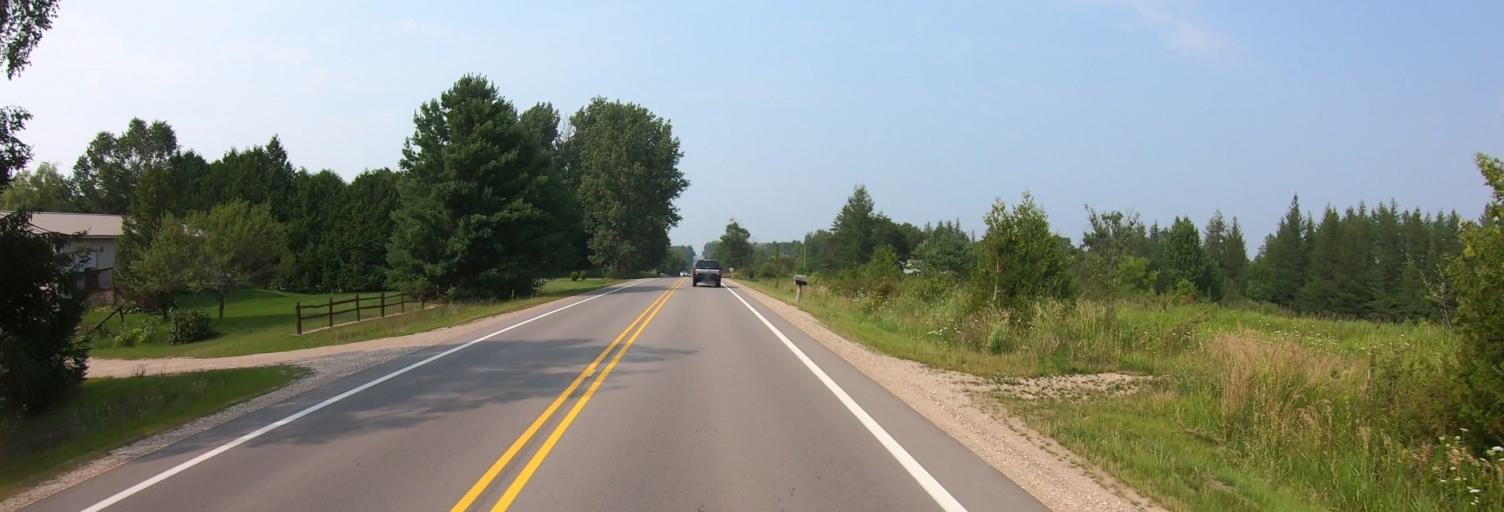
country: US
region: Michigan
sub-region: Charlevoix County
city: Charlevoix
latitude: 45.2329
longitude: -85.2612
